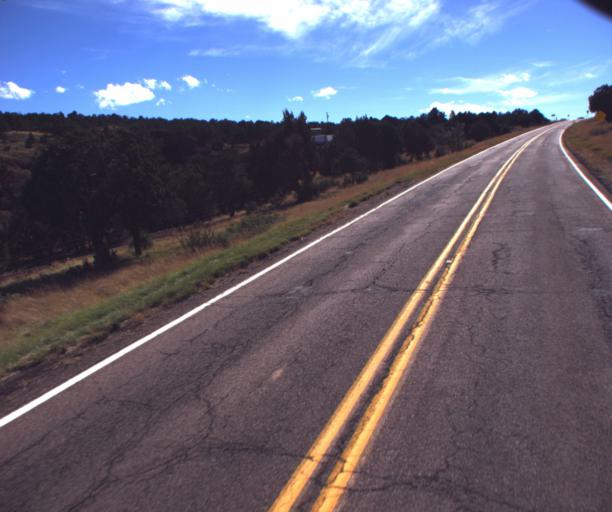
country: US
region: Arizona
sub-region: Navajo County
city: White Mountain Lake
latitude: 34.3116
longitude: -109.7703
